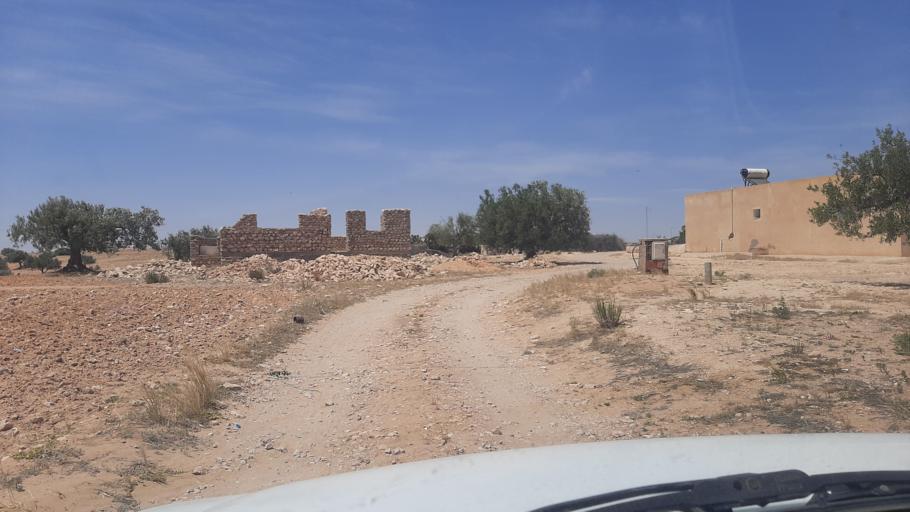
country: TN
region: Safaqis
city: Bi'r `Ali Bin Khalifah
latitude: 34.5675
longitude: 10.3472
